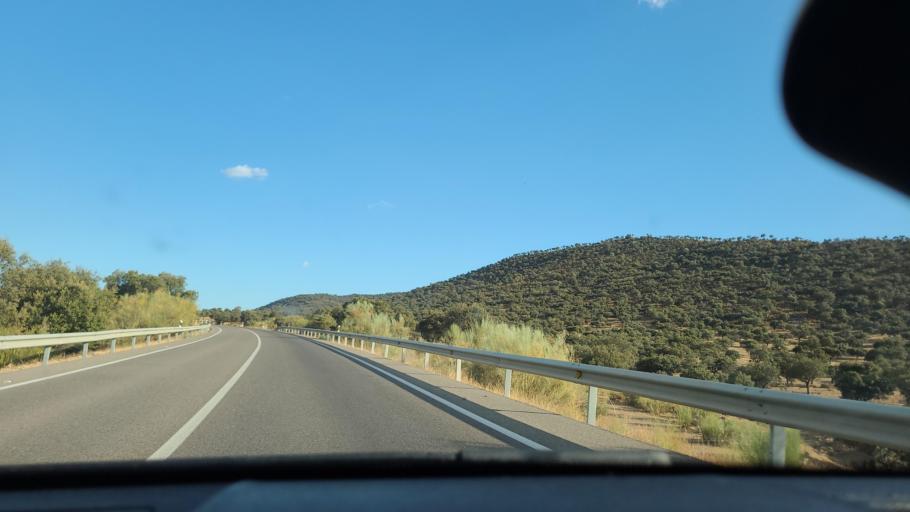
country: ES
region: Andalusia
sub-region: Province of Cordoba
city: Belmez
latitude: 38.2300
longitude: -5.1661
